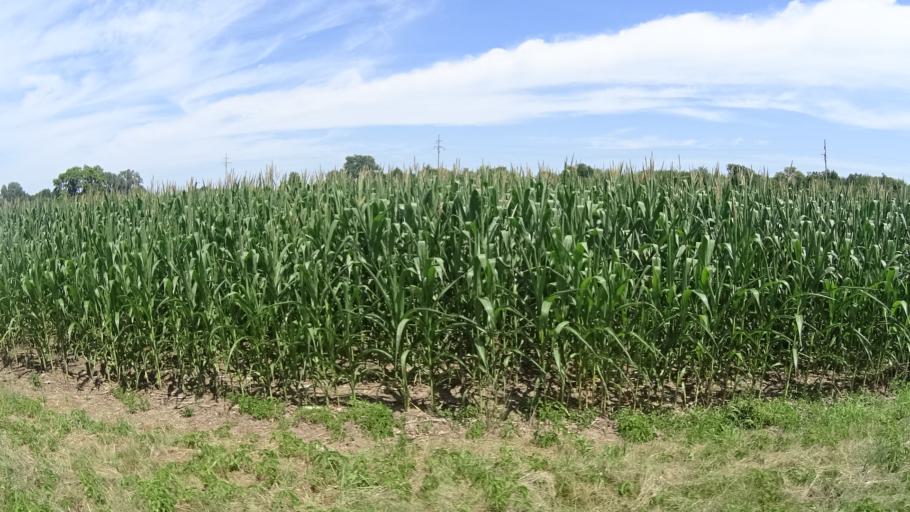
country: US
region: Ohio
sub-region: Erie County
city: Sandusky
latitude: 41.3728
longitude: -82.7700
